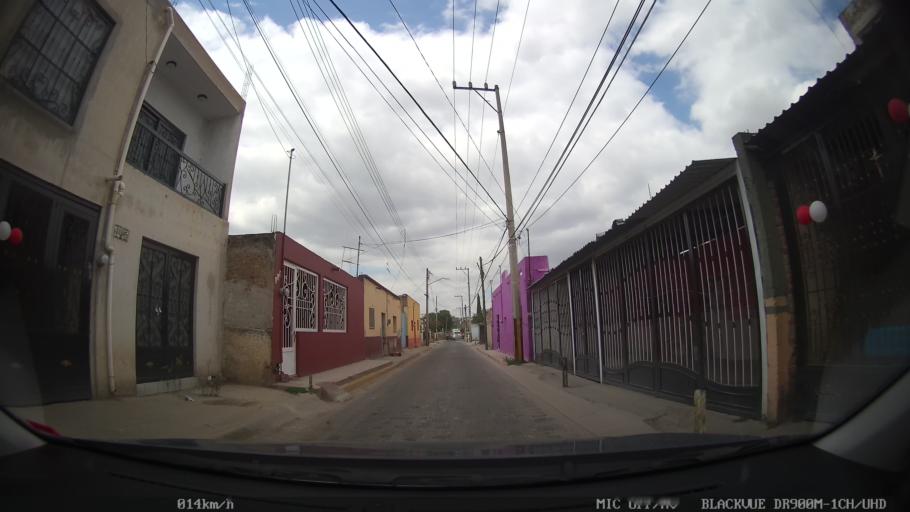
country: MX
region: Jalisco
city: Tlaquepaque
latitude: 20.6425
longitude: -103.2617
